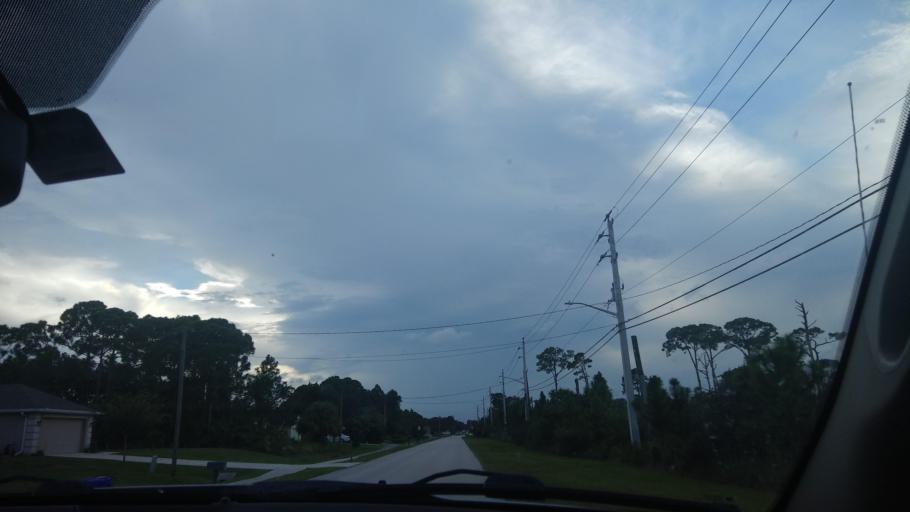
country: US
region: Florida
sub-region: Indian River County
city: Sebastian
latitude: 27.7778
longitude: -80.4714
